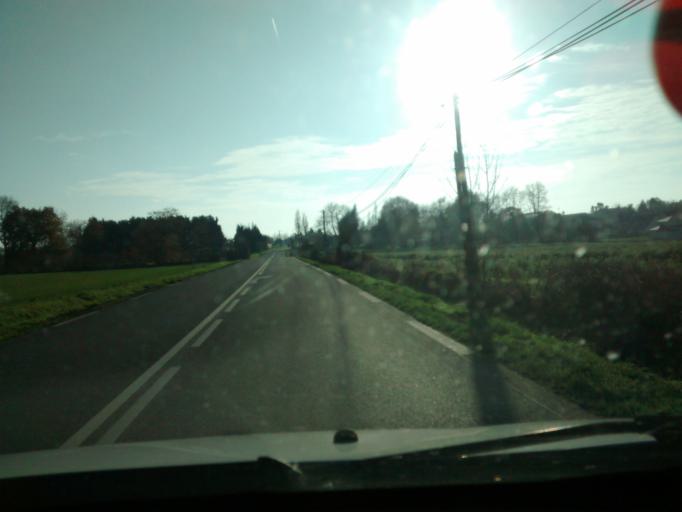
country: FR
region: Brittany
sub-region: Departement d'Ille-et-Vilaine
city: Sens-de-Bretagne
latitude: 48.3365
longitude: -1.5226
